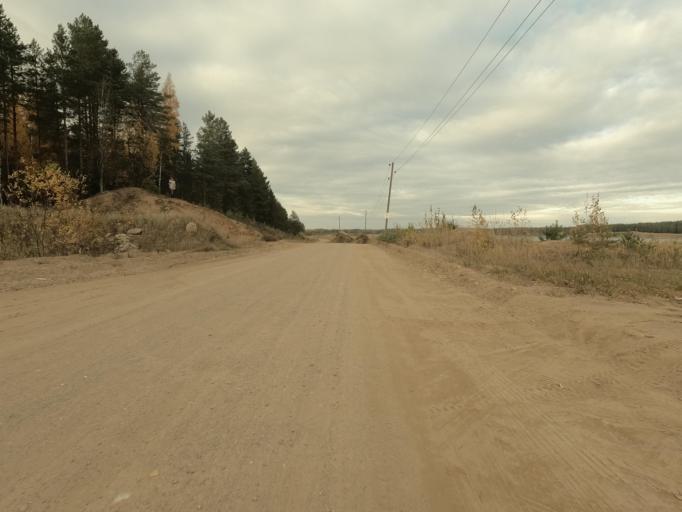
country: RU
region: Leningrad
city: Priladozhskiy
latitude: 59.6986
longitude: 31.3622
